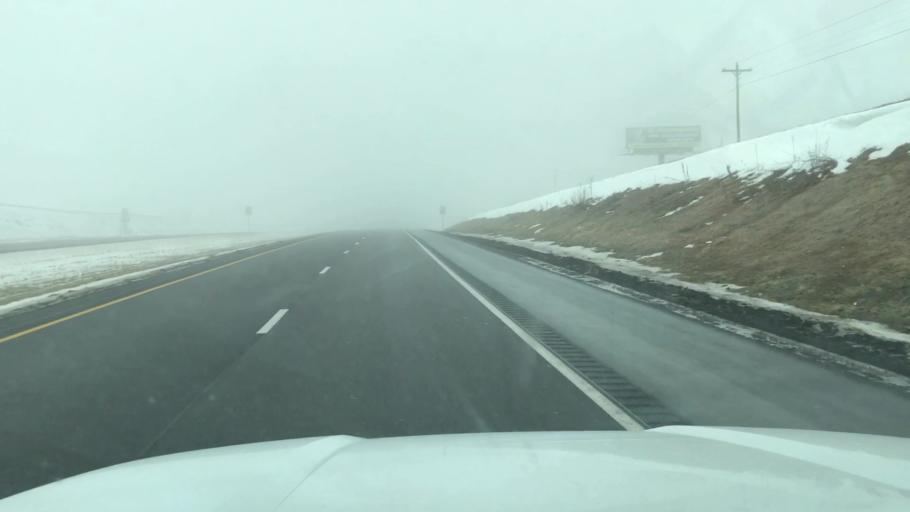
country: US
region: Missouri
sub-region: Clinton County
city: Cameron
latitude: 39.7540
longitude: -94.2585
